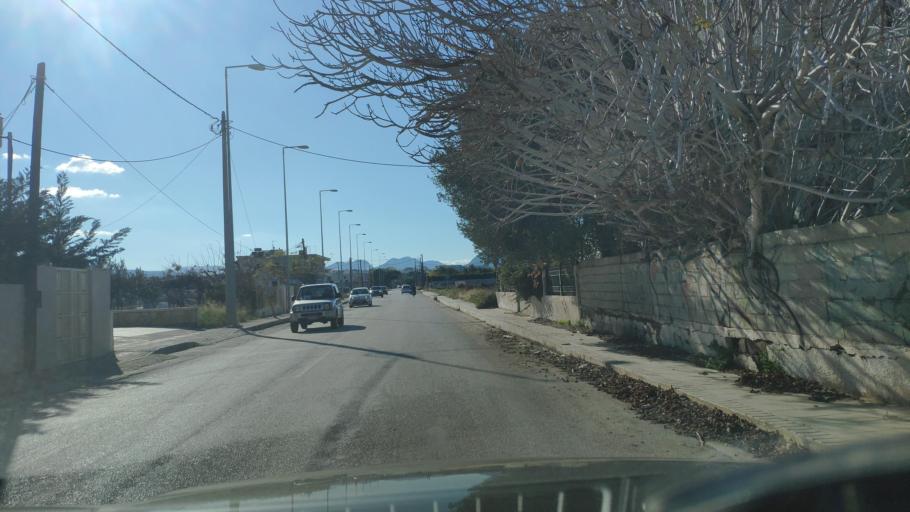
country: GR
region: Peloponnese
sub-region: Nomos Korinthias
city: Korinthos
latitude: 37.9472
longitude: 22.9579
